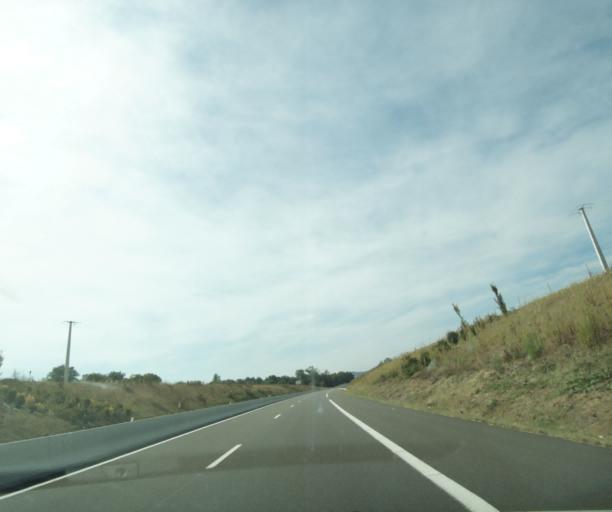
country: FR
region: Auvergne
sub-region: Departement de l'Allier
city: Gannat
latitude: 46.1037
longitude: 3.2534
